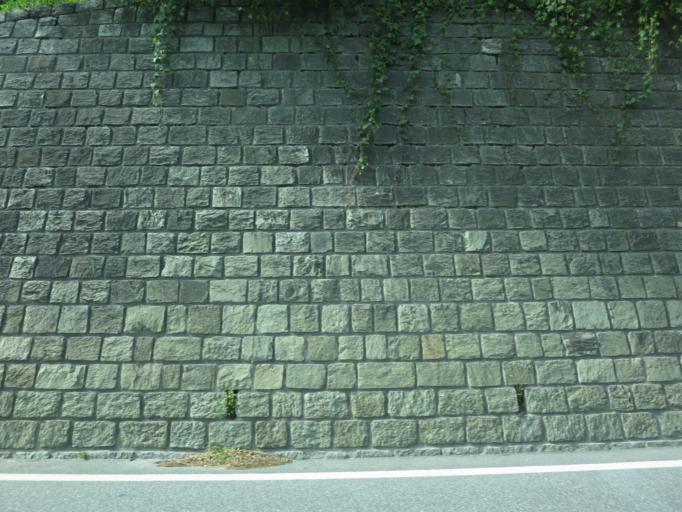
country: CH
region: Grisons
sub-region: Hinterrhein District
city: Thusis
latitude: 46.7029
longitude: 9.4396
